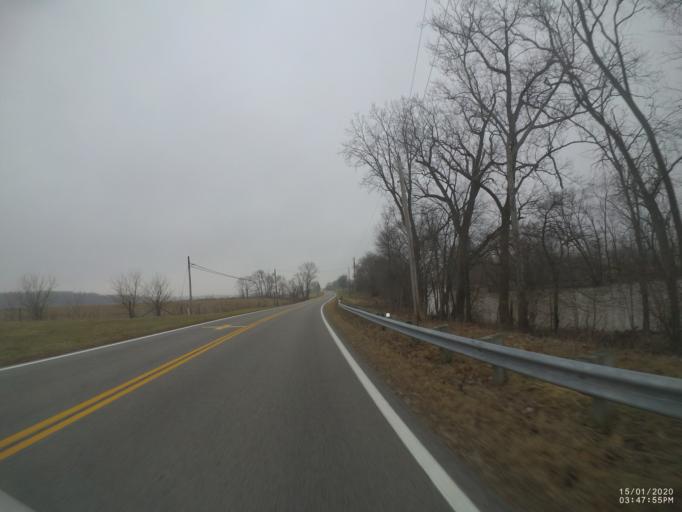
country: US
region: Ohio
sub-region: Sandusky County
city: Woodville
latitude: 41.4374
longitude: -83.3915
